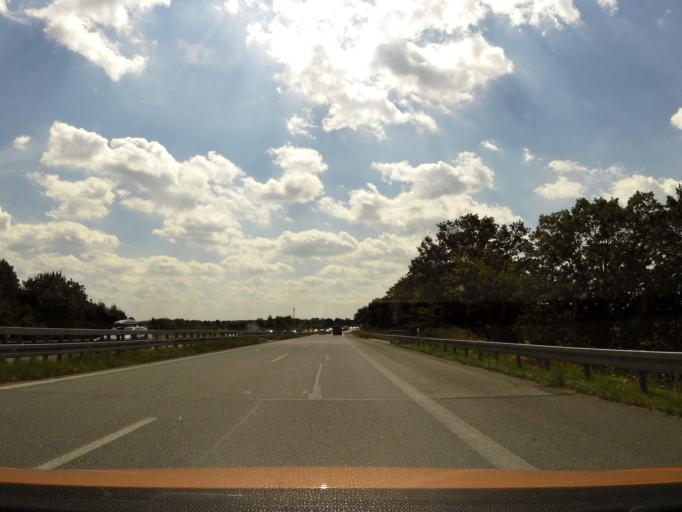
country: DE
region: Brandenburg
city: Althuttendorf
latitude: 52.9807
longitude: 13.8192
